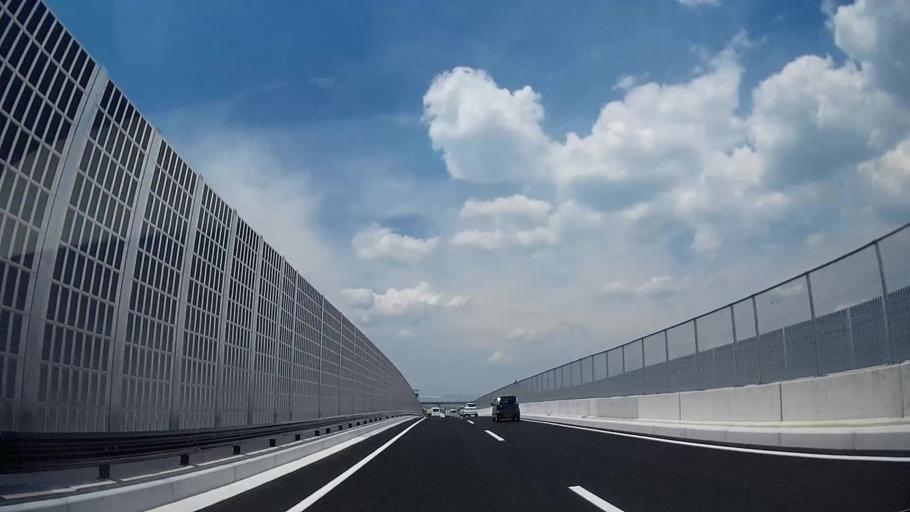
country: JP
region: Chiba
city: Matsudo
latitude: 35.7353
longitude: 139.9201
